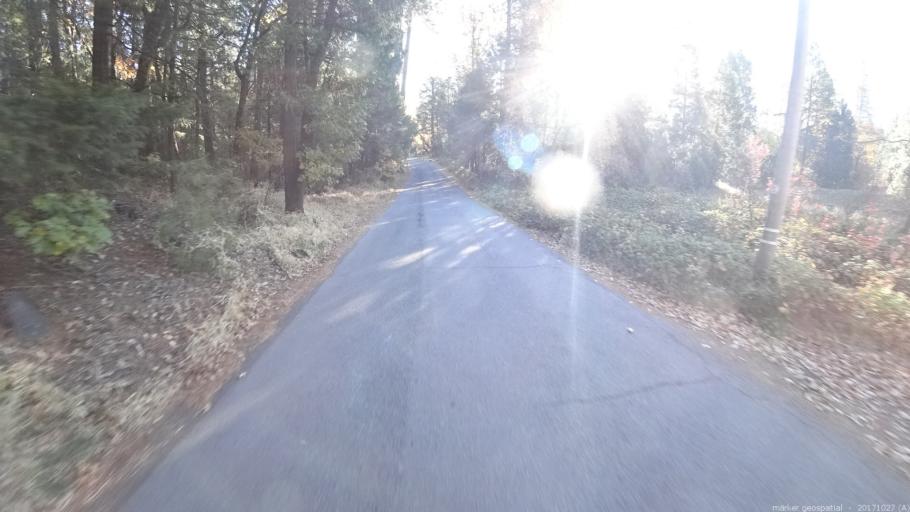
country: US
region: California
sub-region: Shasta County
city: Burney
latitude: 41.0115
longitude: -121.9010
